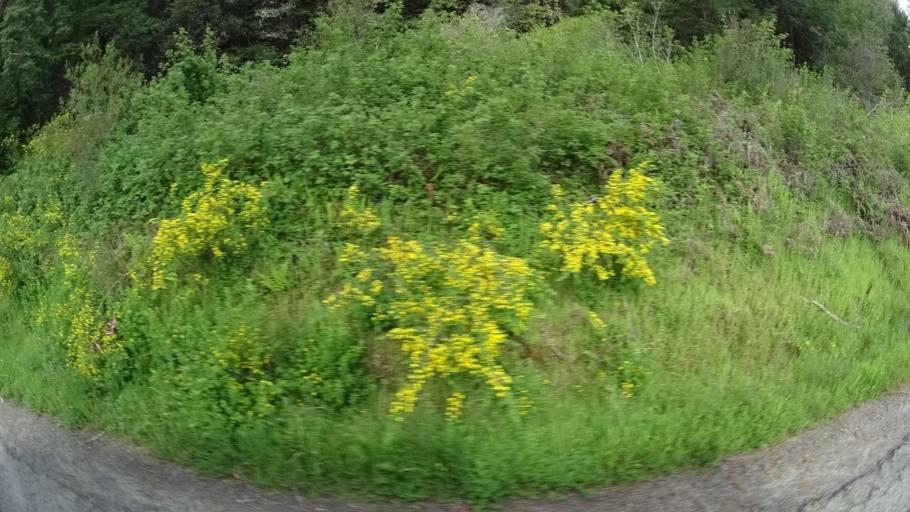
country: US
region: California
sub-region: Humboldt County
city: Redway
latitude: 40.2468
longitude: -123.8329
